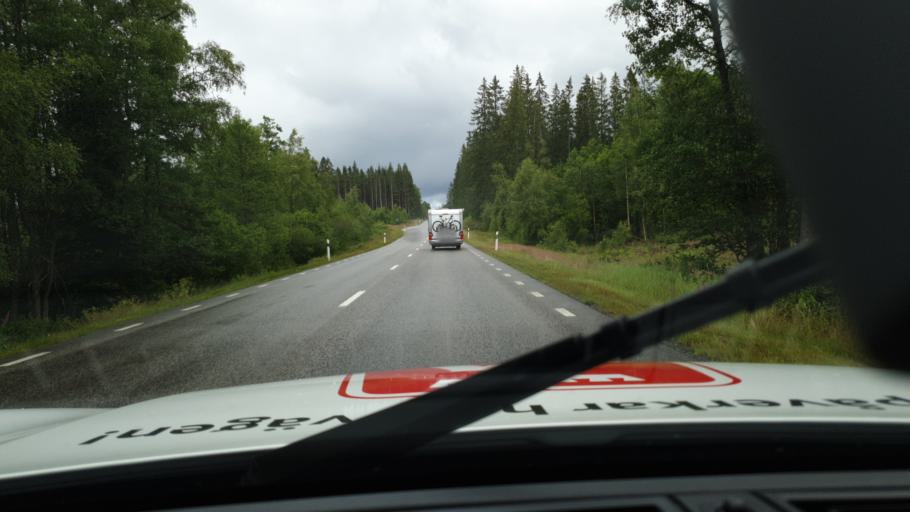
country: SE
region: Kronoberg
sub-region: Vaxjo Kommun
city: Lammhult
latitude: 57.1185
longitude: 14.6321
